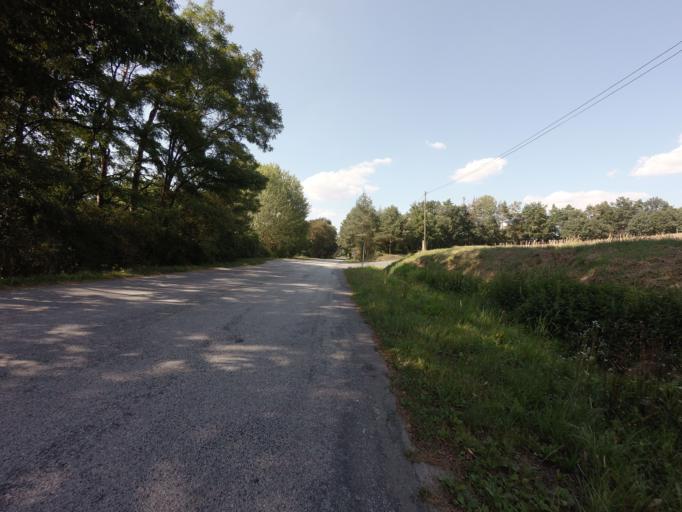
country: CZ
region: Jihocesky
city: Tyn nad Vltavou
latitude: 49.1990
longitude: 14.4458
